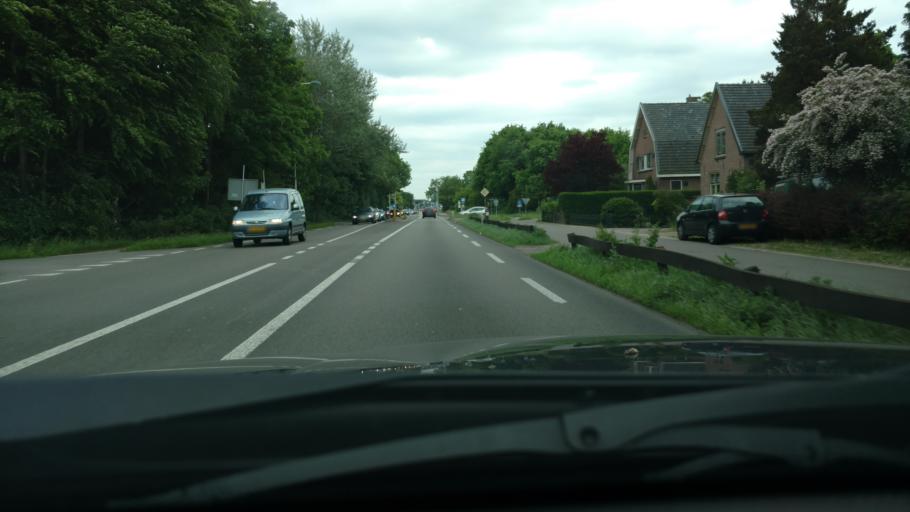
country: NL
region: Gelderland
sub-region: Gemeente Lochem
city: Epse
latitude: 52.2310
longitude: 6.1871
